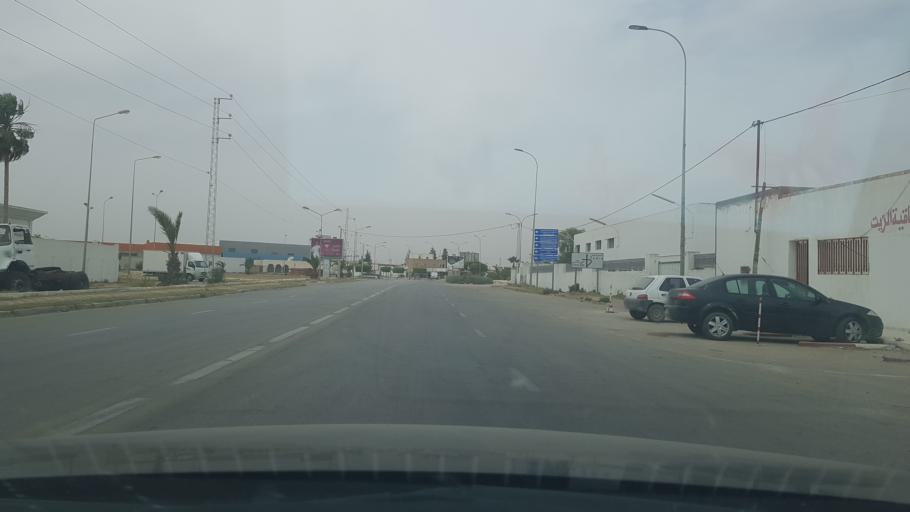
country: TN
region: Safaqis
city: Al Qarmadah
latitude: 34.8354
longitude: 10.7648
